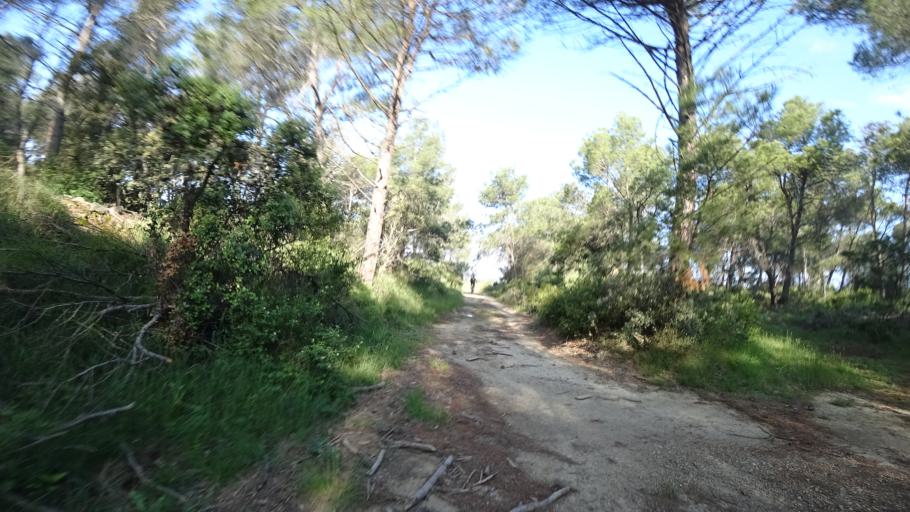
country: FR
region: Languedoc-Roussillon
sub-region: Departement de l'Aude
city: Lezignan-Corbieres
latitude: 43.2372
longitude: 2.7467
